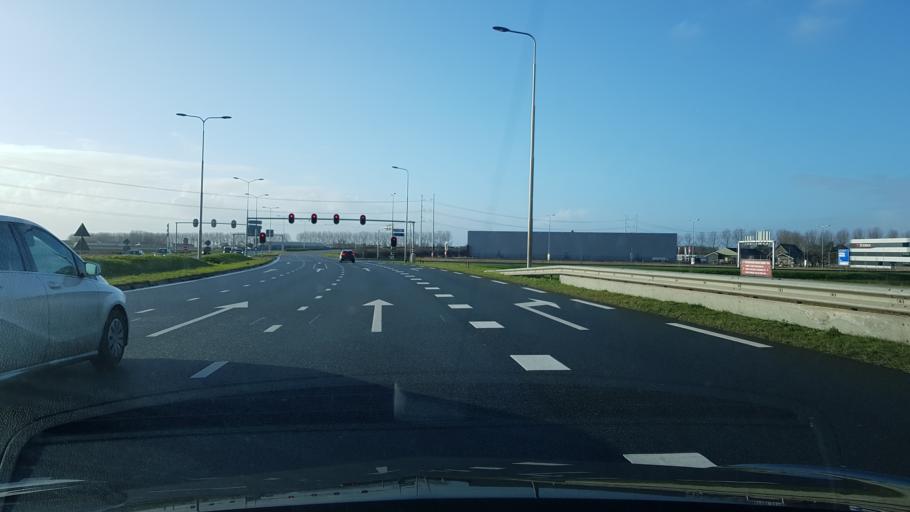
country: NL
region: South Holland
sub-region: Gemeente Kaag en Braassem
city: Oude Wetering
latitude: 52.2522
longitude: 4.6268
